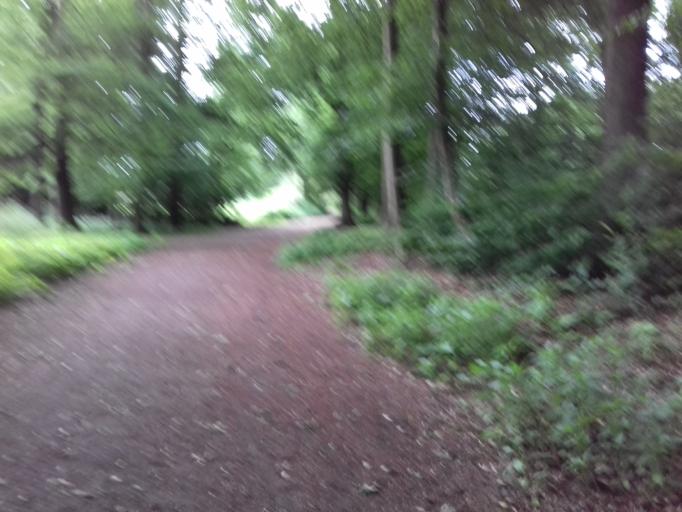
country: DE
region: Schleswig-Holstein
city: Tasdorf
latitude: 54.0807
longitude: 10.0148
